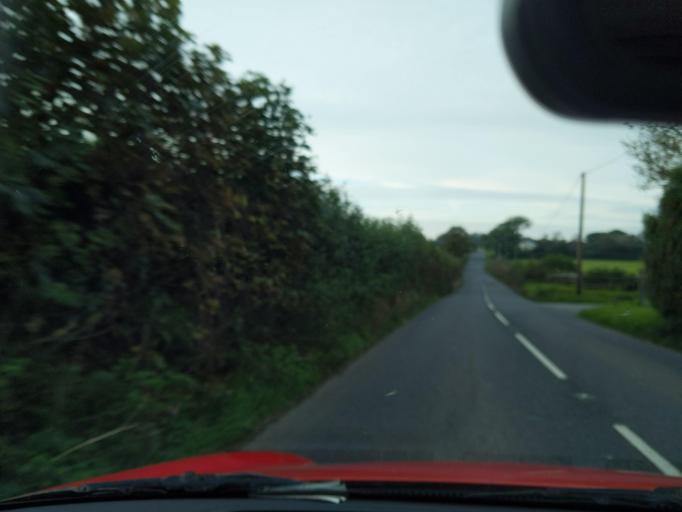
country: GB
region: England
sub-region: Devon
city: Great Torrington
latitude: 50.9291
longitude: -4.1504
